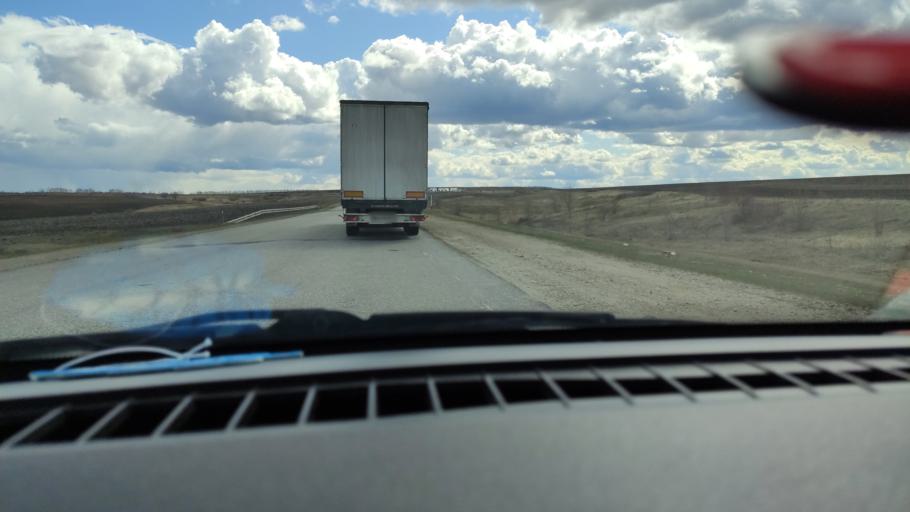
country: RU
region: Samara
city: Syzran'
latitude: 53.0090
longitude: 48.3323
